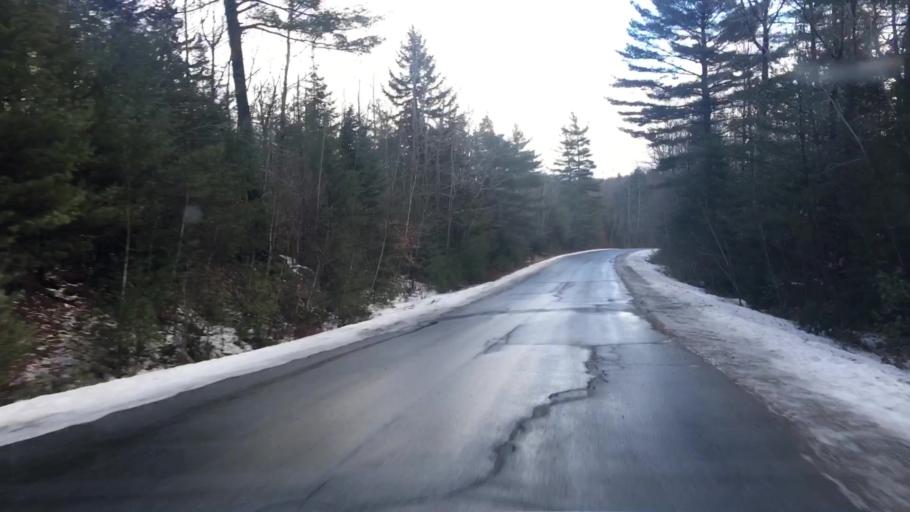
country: US
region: Maine
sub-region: Hancock County
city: Dedham
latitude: 44.6900
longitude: -68.7179
